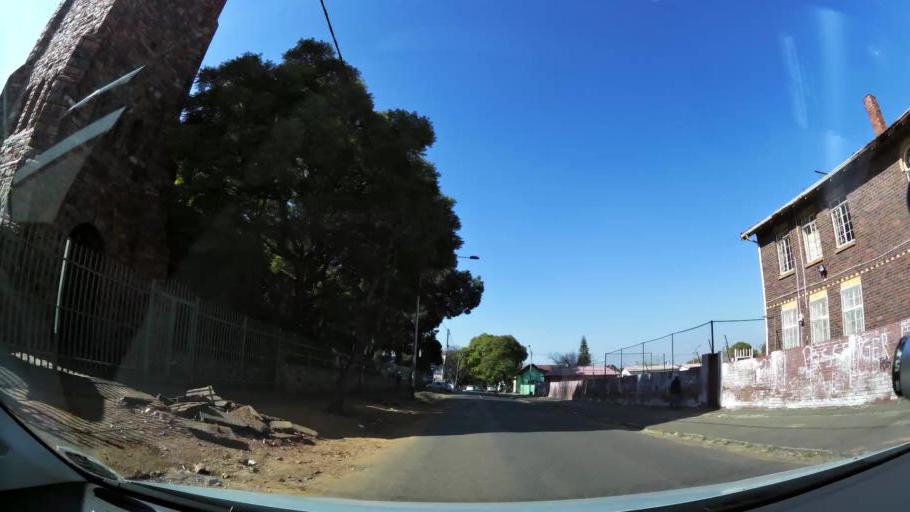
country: ZA
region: Gauteng
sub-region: City of Johannesburg Metropolitan Municipality
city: Johannesburg
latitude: -26.1784
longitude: 28.0655
